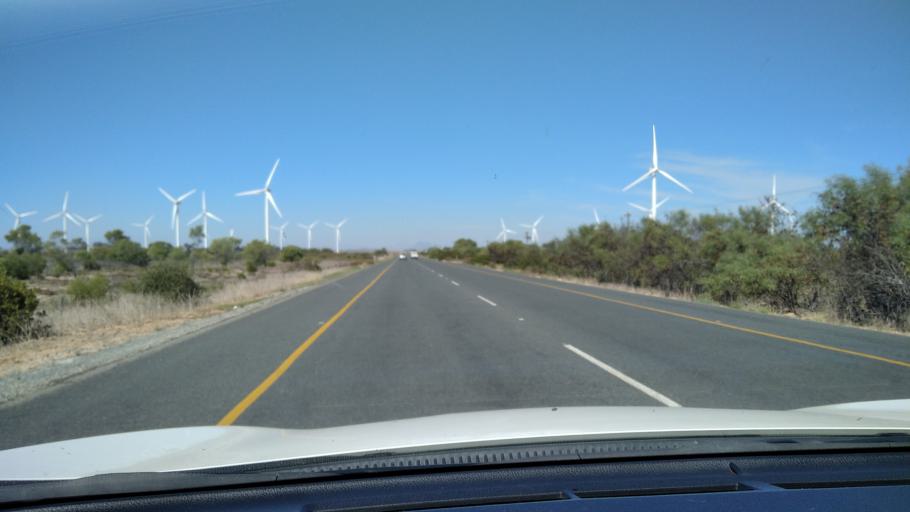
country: ZA
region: Western Cape
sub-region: West Coast District Municipality
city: Moorreesburg
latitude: -33.0786
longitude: 18.3858
